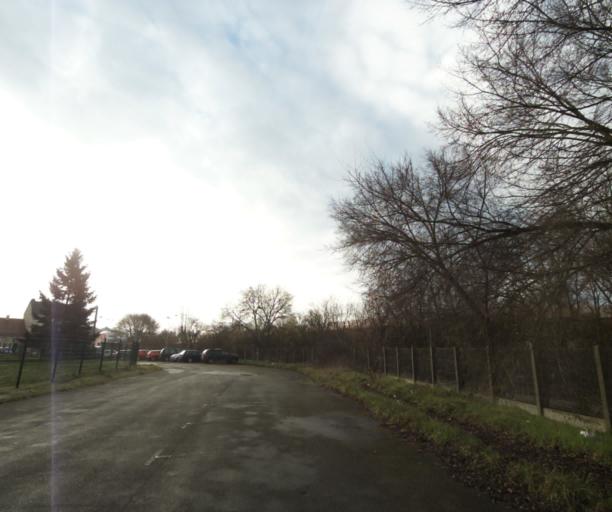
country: FR
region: Pays de la Loire
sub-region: Departement de la Sarthe
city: Le Mans
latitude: 47.9876
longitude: 0.1820
